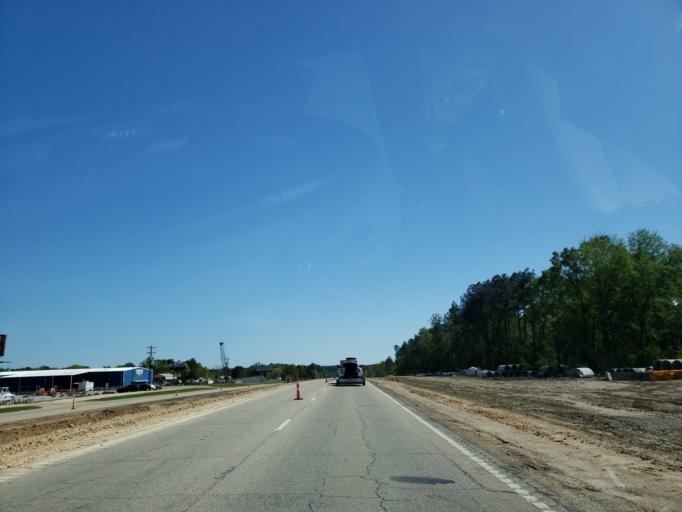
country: US
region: Mississippi
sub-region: Lamar County
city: Purvis
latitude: 31.0696
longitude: -89.2092
